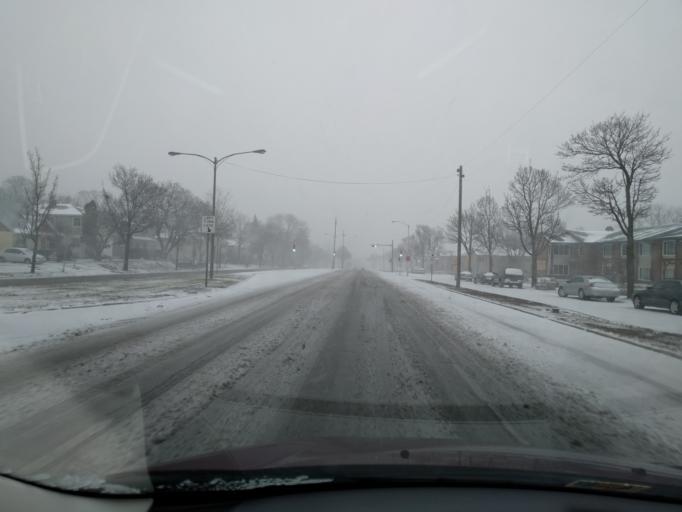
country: US
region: Wisconsin
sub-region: Milwaukee County
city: Brown Deer
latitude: 43.1195
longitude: -88.0023
